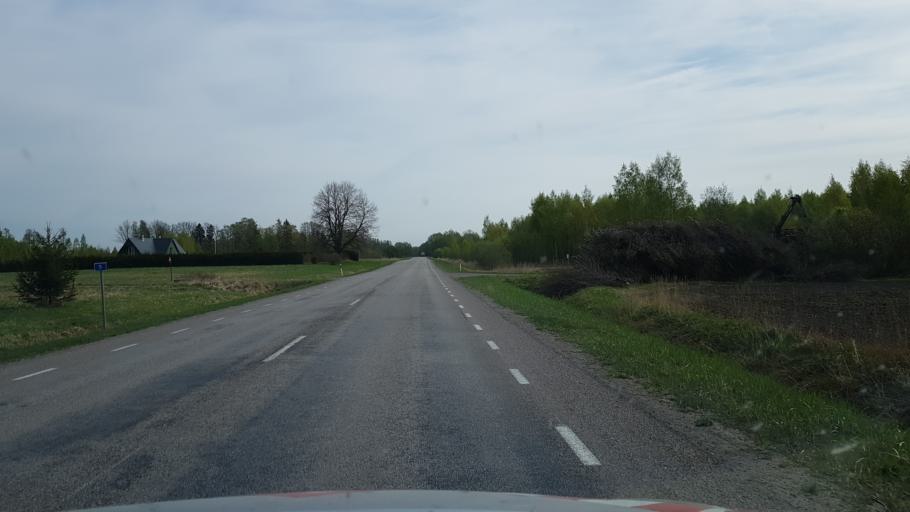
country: EE
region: Paernumaa
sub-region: Audru vald
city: Audru
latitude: 58.3958
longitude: 24.2865
